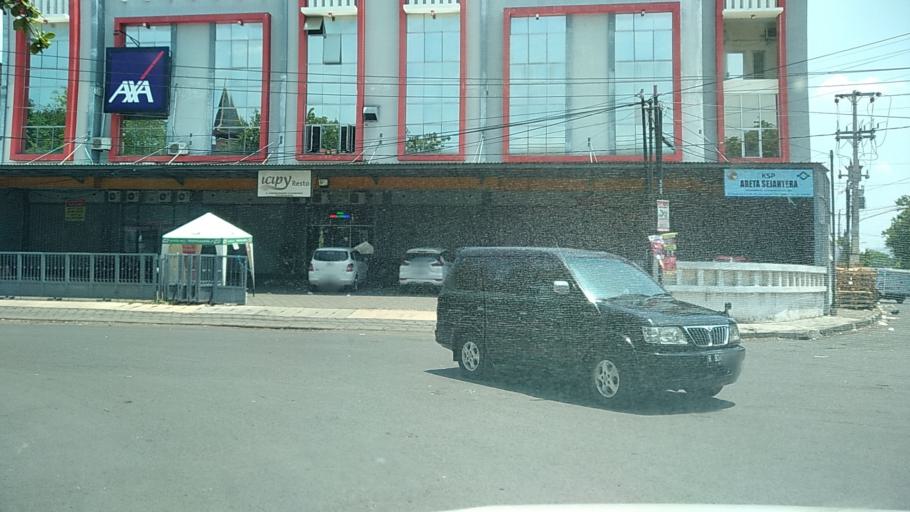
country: ID
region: Central Java
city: Semarang
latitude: -6.9807
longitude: 110.4290
